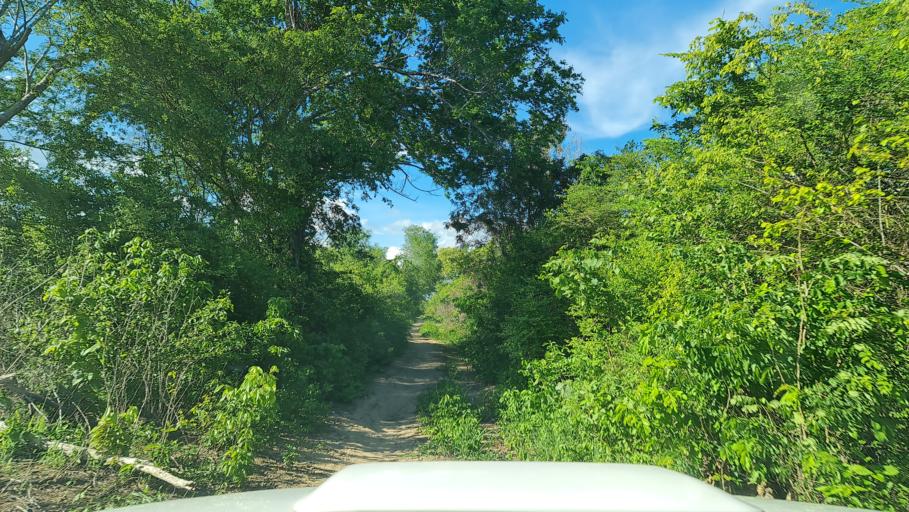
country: MZ
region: Nampula
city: Ilha de Mocambique
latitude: -15.2625
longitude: 40.1853
